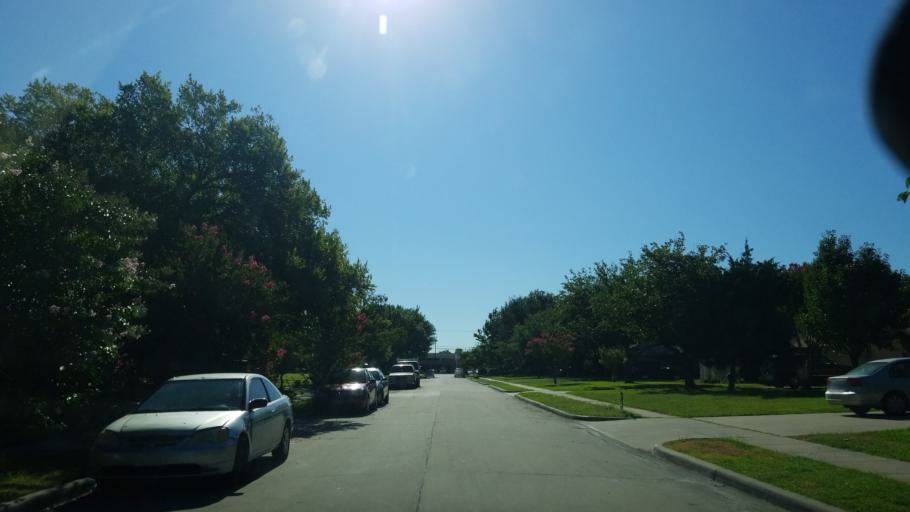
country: US
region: Texas
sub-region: Dallas County
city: Carrollton
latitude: 32.9501
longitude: -96.8925
